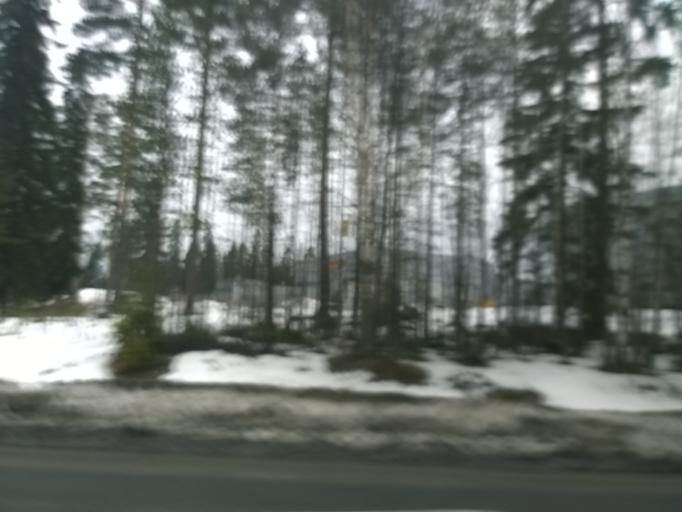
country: FI
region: Pirkanmaa
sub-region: Tampere
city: Tampere
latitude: 61.4184
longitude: 23.7560
